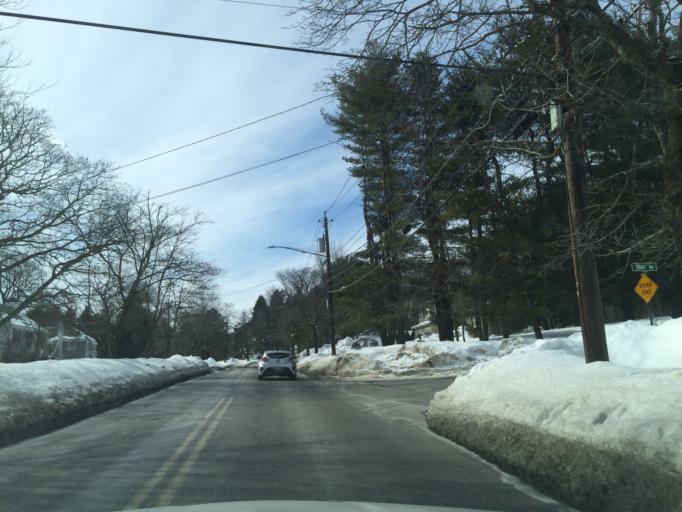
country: US
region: Massachusetts
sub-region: Middlesex County
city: Newton
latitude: 42.3003
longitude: -71.1843
